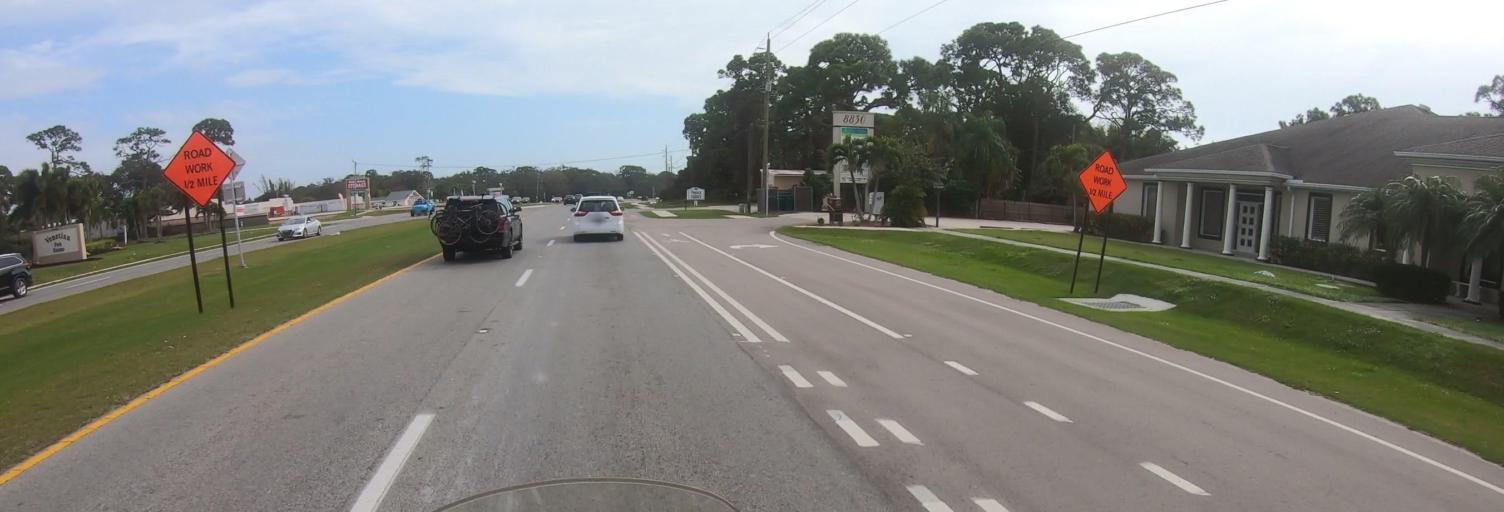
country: US
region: Florida
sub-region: Sarasota County
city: Vamo
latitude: 27.2214
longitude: -82.4920
